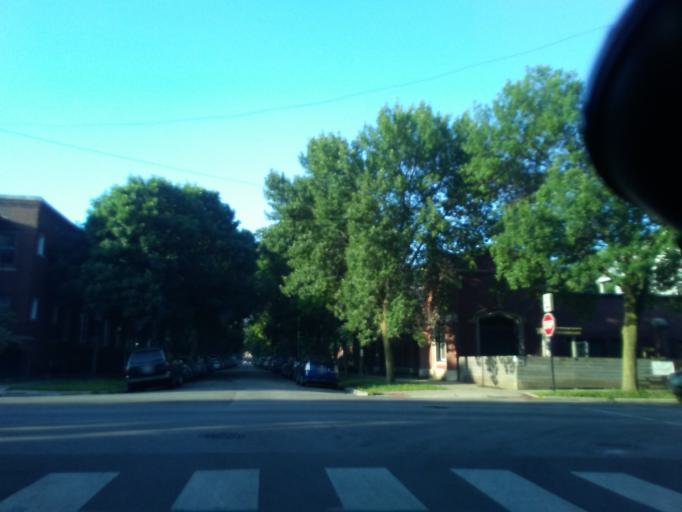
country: US
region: Illinois
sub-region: Cook County
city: Lincolnwood
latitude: 41.9284
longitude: -87.7159
